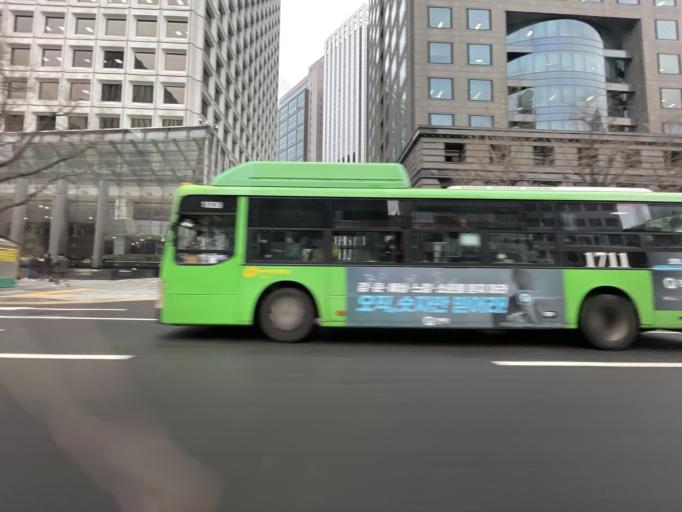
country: KR
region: Seoul
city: Seoul
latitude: 37.5627
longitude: 126.9764
